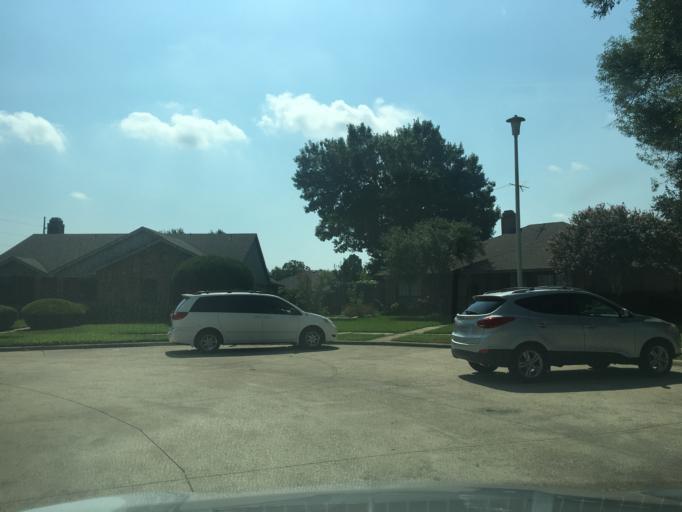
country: US
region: Texas
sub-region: Dallas County
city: Sachse
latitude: 32.9506
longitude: -96.6253
